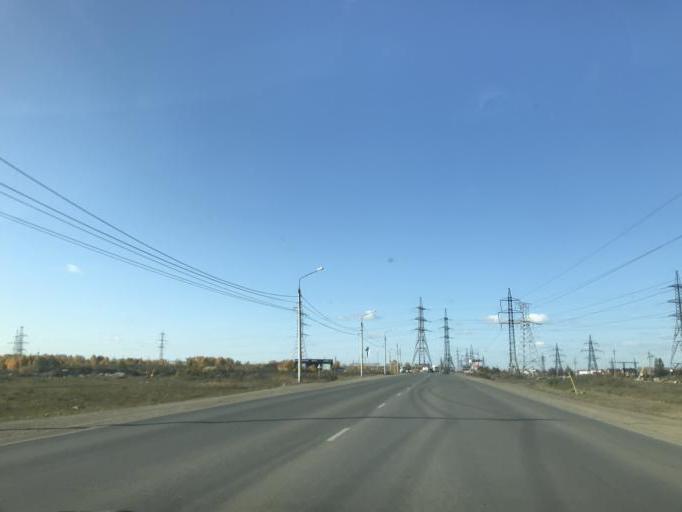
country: RU
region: Chelyabinsk
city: Roshchino
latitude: 55.2232
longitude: 61.2932
